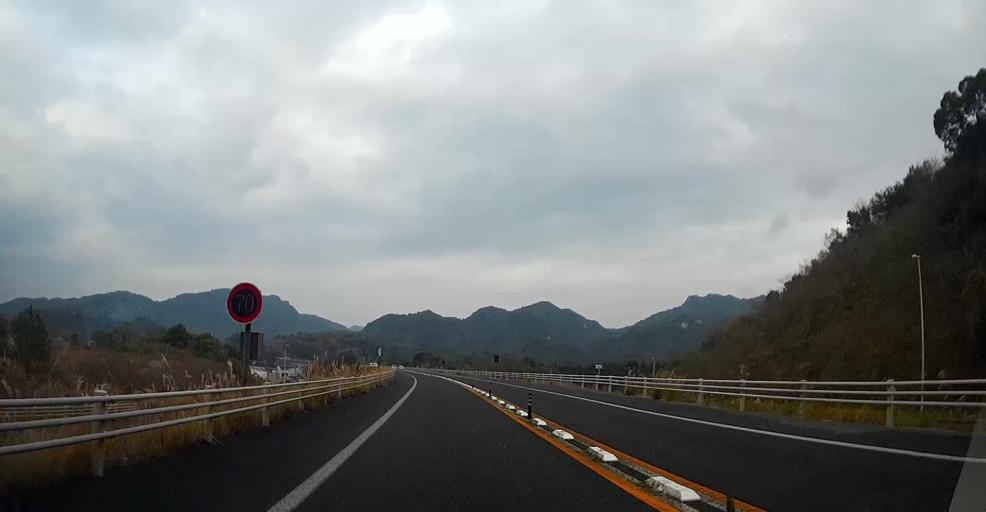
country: JP
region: Kumamoto
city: Hondo
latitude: 32.4968
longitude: 130.3901
